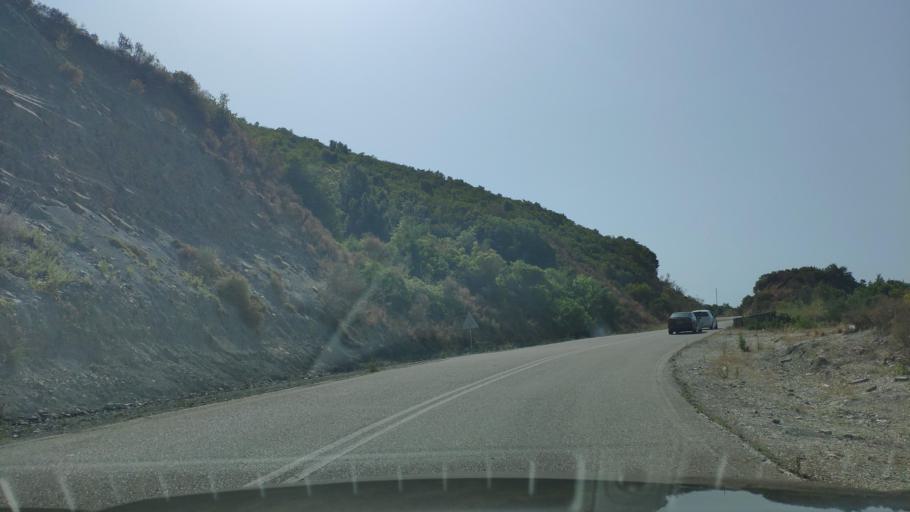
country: GR
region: Epirus
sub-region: Nomos Artas
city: Peta
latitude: 39.1708
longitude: 21.0619
